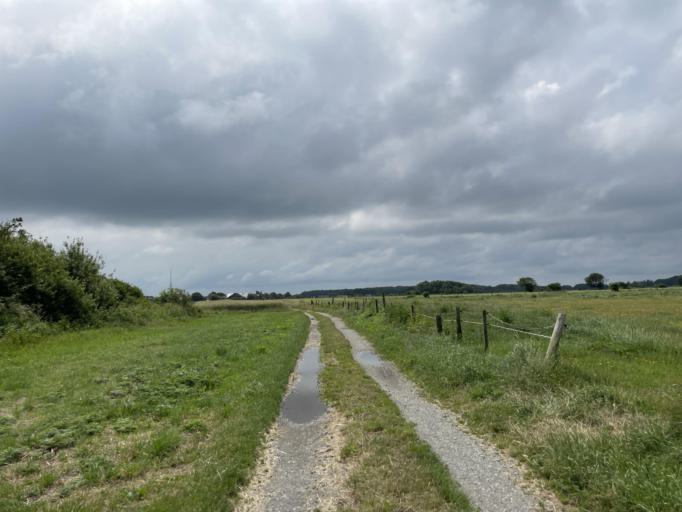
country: DE
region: Lower Saxony
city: Cuxhaven
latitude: 53.8783
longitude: 8.6449
